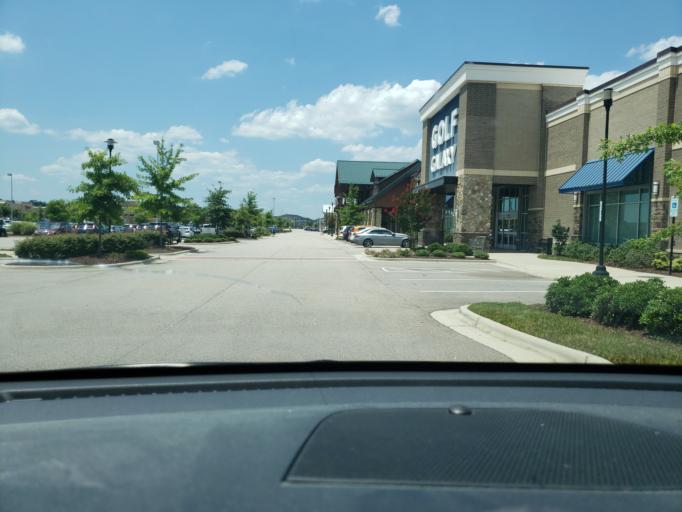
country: US
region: North Carolina
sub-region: Wake County
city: Morrisville
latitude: 35.8471
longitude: -78.8870
